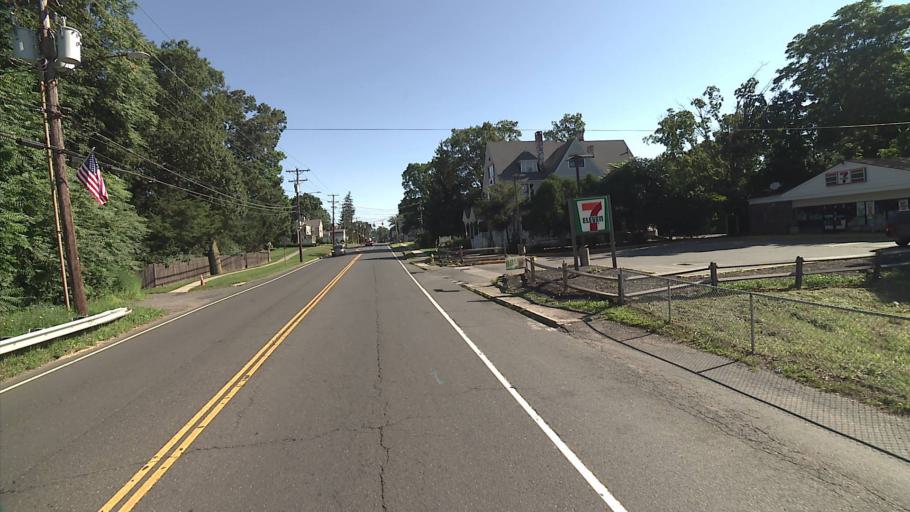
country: US
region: Connecticut
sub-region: New Haven County
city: Cheshire
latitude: 41.4951
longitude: -72.9033
